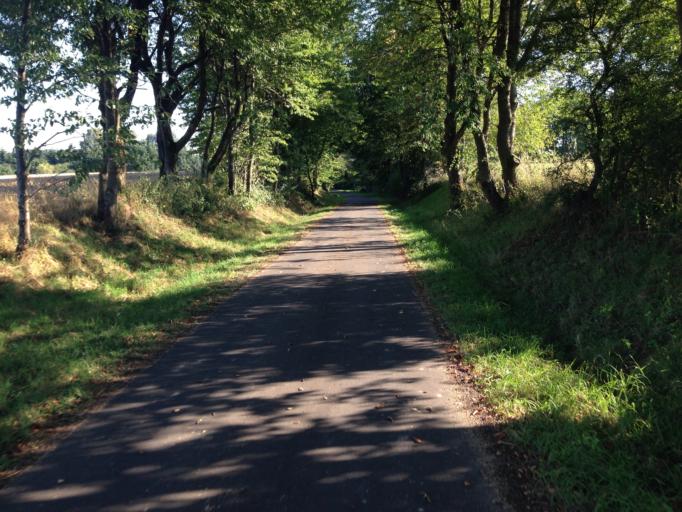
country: DE
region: Hesse
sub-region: Regierungsbezirk Giessen
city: Grunberg
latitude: 50.6047
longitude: 8.9645
